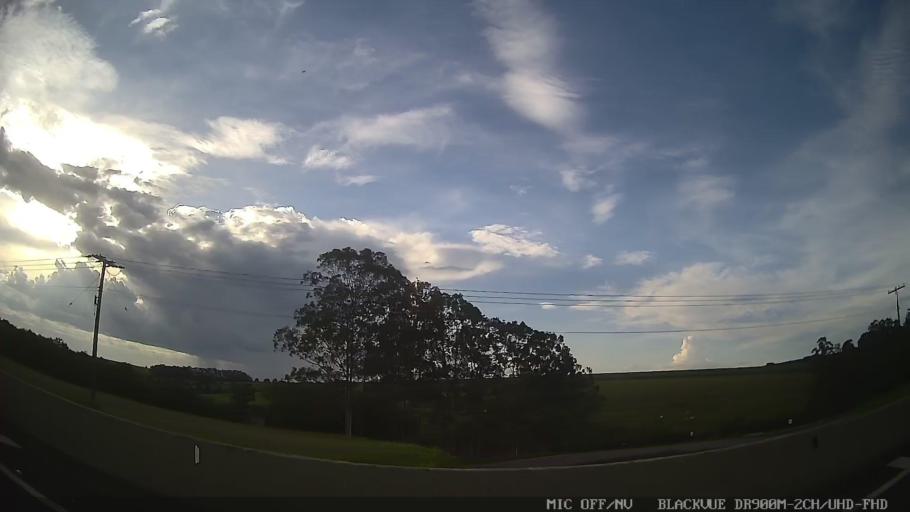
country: BR
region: Sao Paulo
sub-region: Tiete
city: Tiete
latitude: -23.0609
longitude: -47.7241
